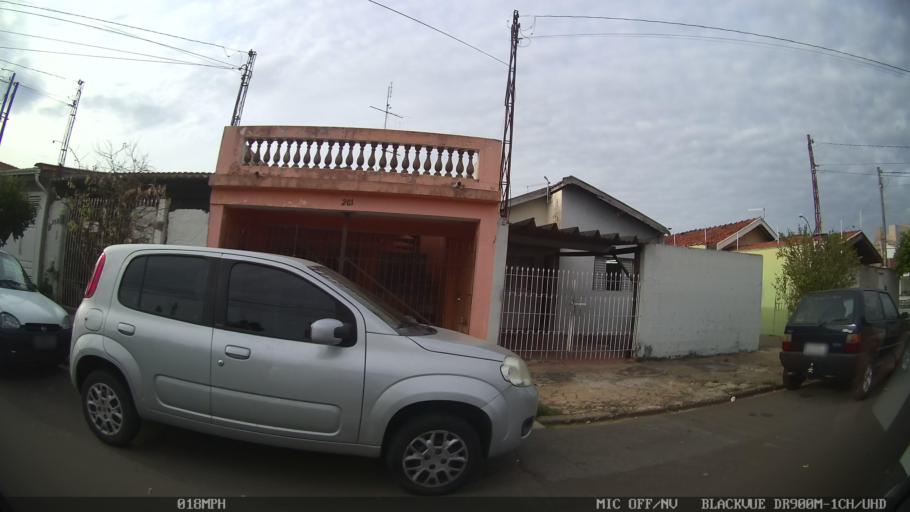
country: BR
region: Sao Paulo
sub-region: Piracicaba
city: Piracicaba
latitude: -22.7331
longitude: -47.6262
